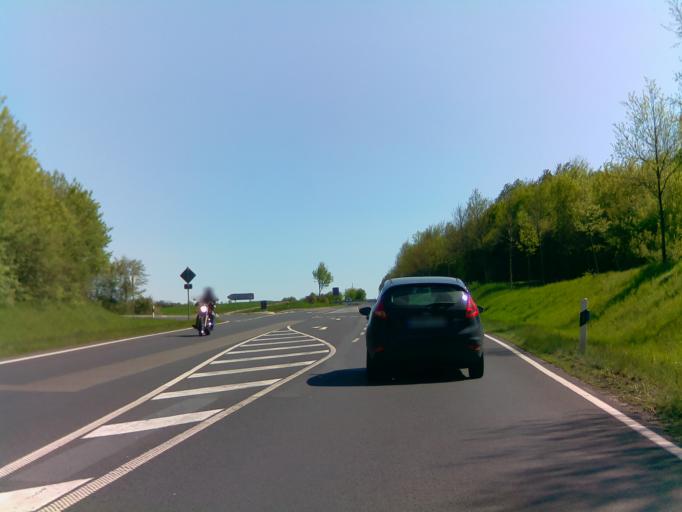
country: DE
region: Hesse
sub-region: Regierungsbezirk Giessen
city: Lauterbach
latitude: 50.6929
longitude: 9.3417
